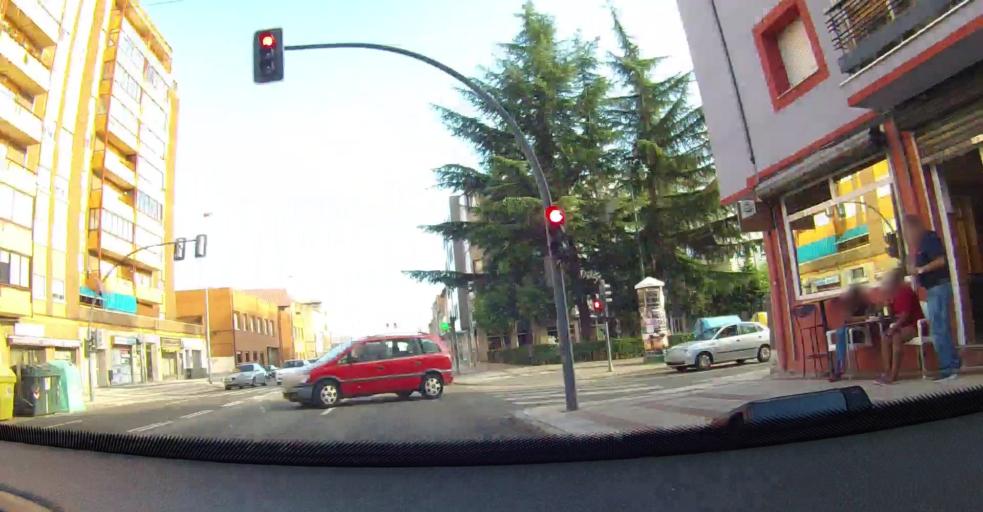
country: ES
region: Castille and Leon
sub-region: Provincia de Leon
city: Leon
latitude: 42.5967
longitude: -5.5854
